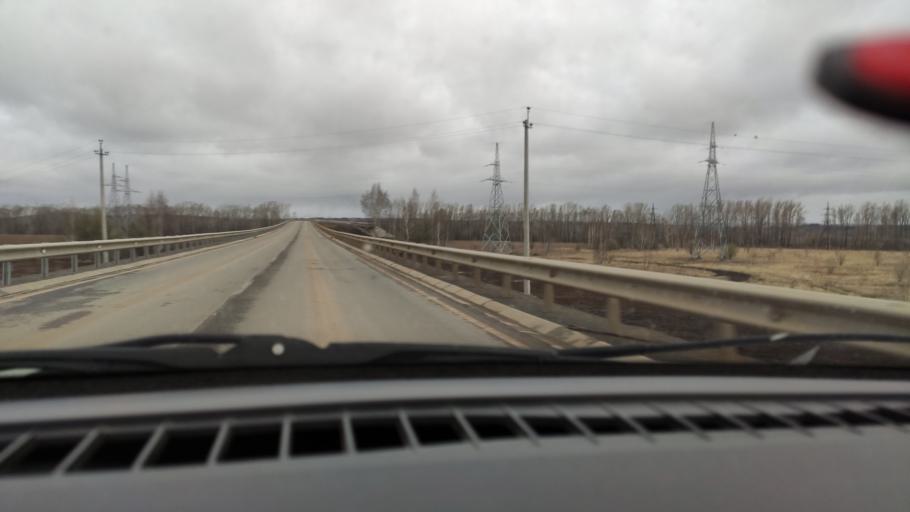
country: RU
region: Perm
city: Kuyeda
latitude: 56.4166
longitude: 55.5540
